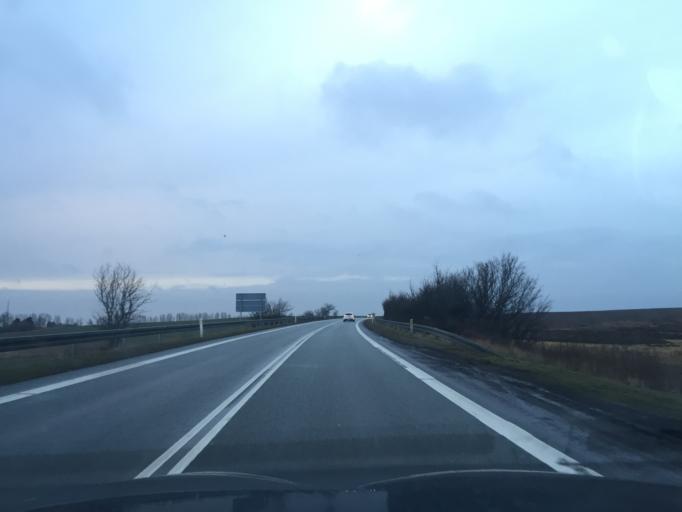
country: DK
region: Zealand
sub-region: Slagelse Kommune
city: Slagelse
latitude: 55.3736
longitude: 11.3288
